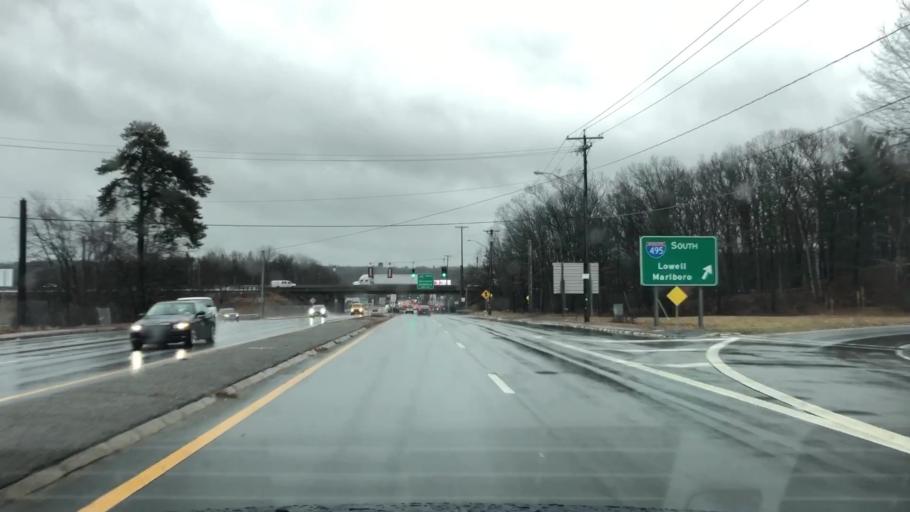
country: US
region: Massachusetts
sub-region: Essex County
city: North Andover
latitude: 42.6874
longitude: -71.1450
